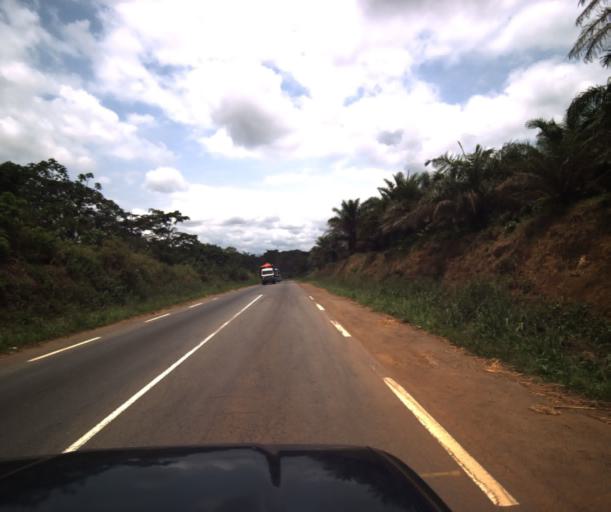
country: CM
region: Centre
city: Eseka
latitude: 3.8672
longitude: 10.9192
